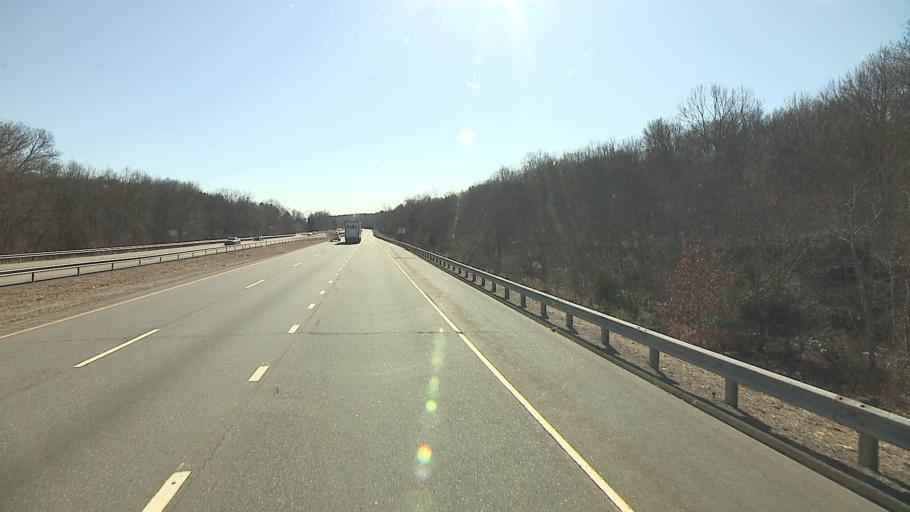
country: US
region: Connecticut
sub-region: New London County
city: Colchester
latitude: 41.5890
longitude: -72.3889
